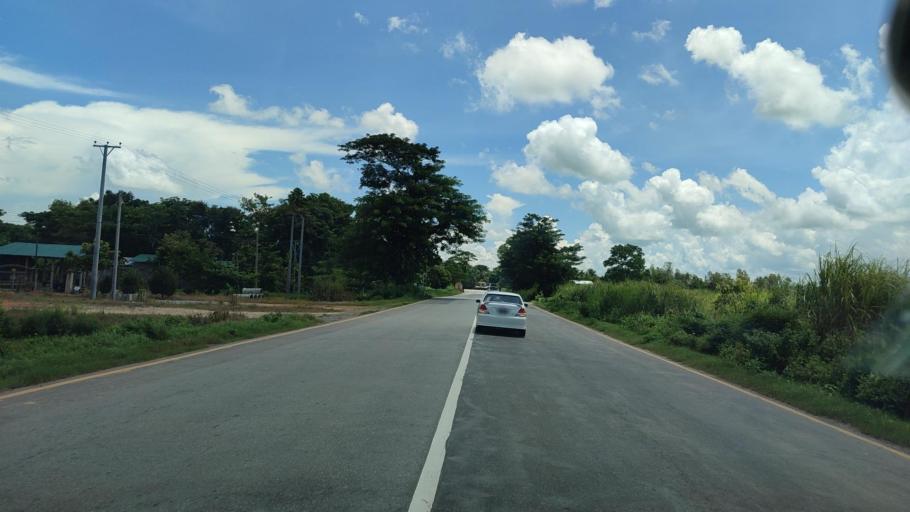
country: MM
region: Bago
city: Nyaunglebin
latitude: 18.2048
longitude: 96.5626
